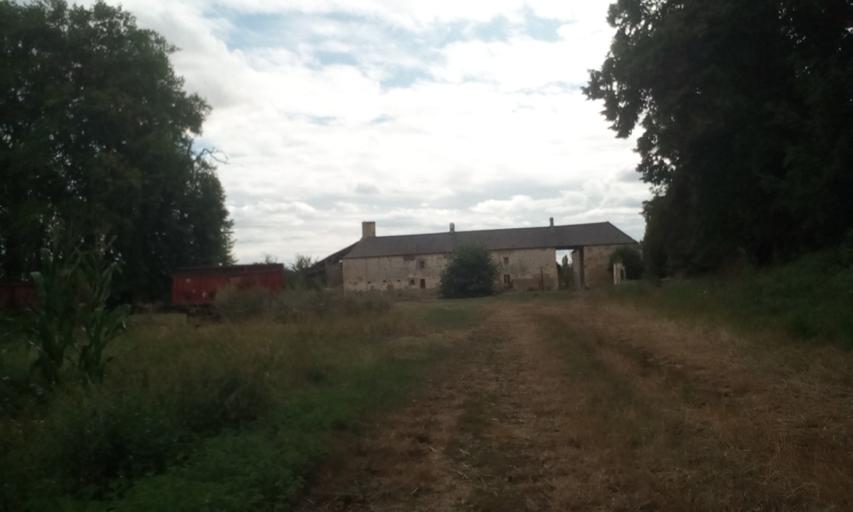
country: FR
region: Lower Normandy
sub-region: Departement du Calvados
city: Bellengreville
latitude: 49.1247
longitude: -0.2027
